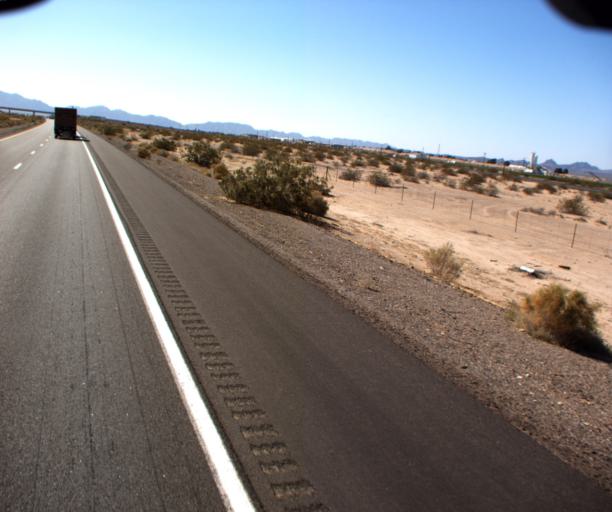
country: US
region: Arizona
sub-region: Yuma County
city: Wellton
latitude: 32.6718
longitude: -114.1005
